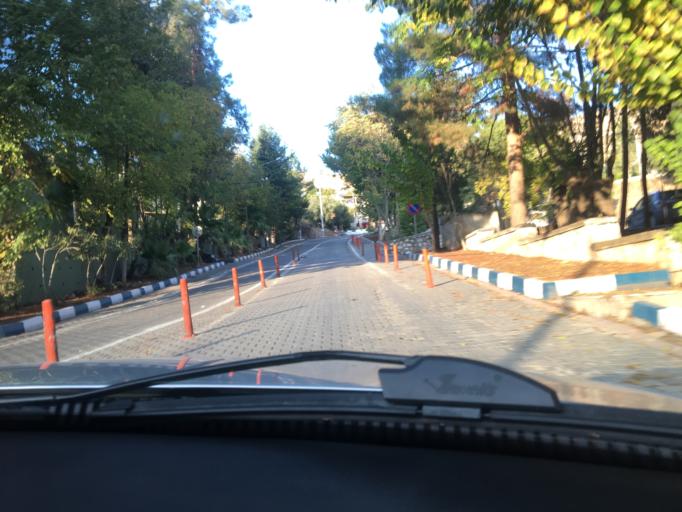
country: TR
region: Sanliurfa
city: Halfeti
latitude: 37.2432
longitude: 37.8705
